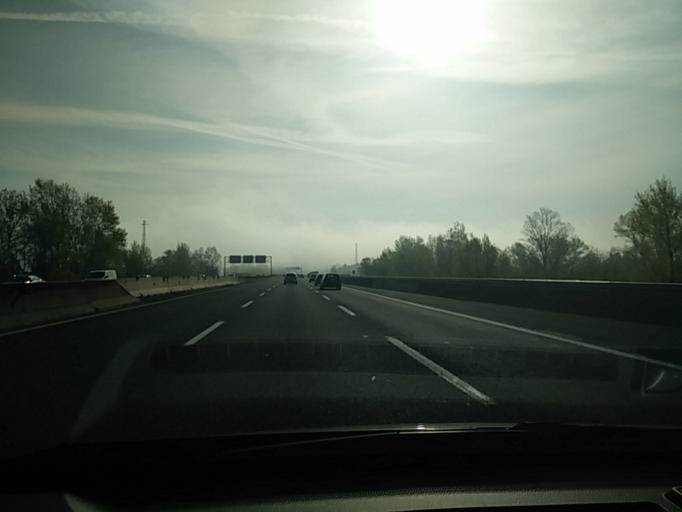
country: IT
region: Emilia-Romagna
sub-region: Provincia di Bologna
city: Villanova
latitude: 44.4805
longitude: 11.4367
